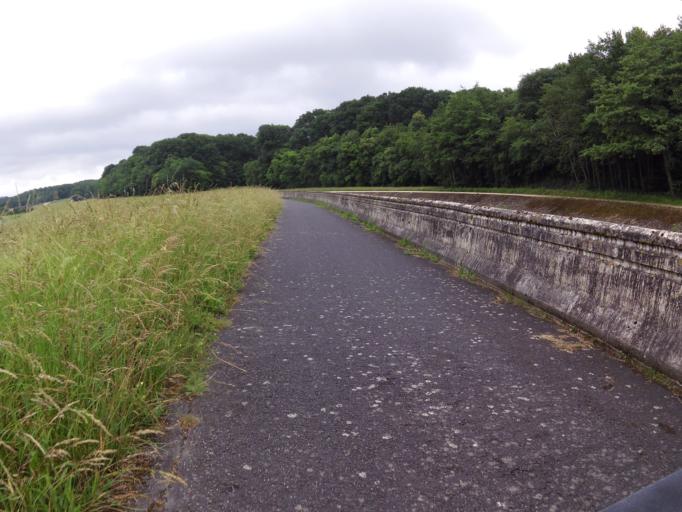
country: FR
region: Champagne-Ardenne
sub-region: Departement de la Haute-Marne
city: Villiers-en-Lieu
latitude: 48.6160
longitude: 4.8960
